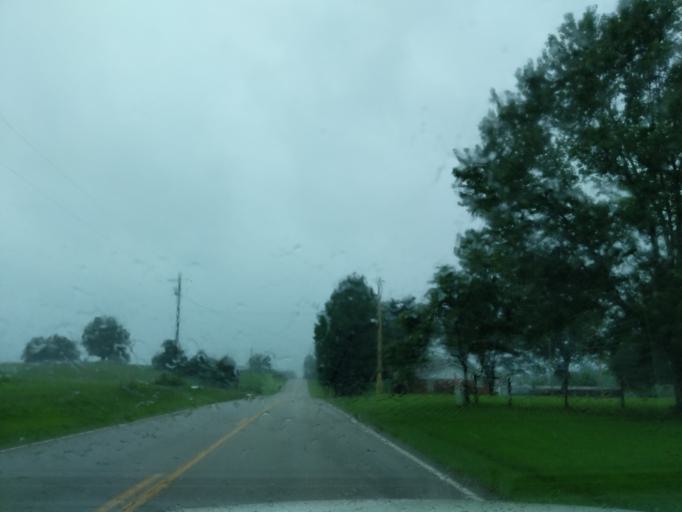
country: US
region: Kentucky
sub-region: Barren County
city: Cave City
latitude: 37.1329
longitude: -86.0441
